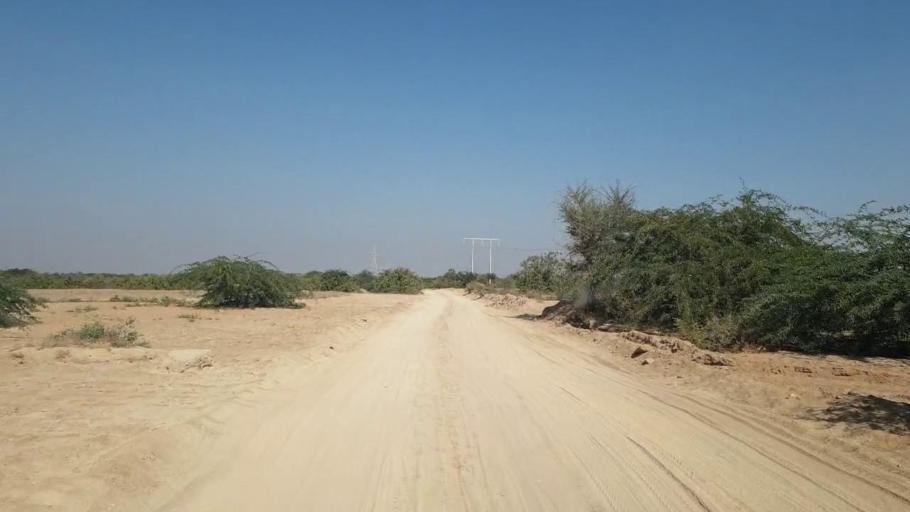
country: PK
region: Sindh
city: Jamshoro
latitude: 25.3060
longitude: 67.8168
